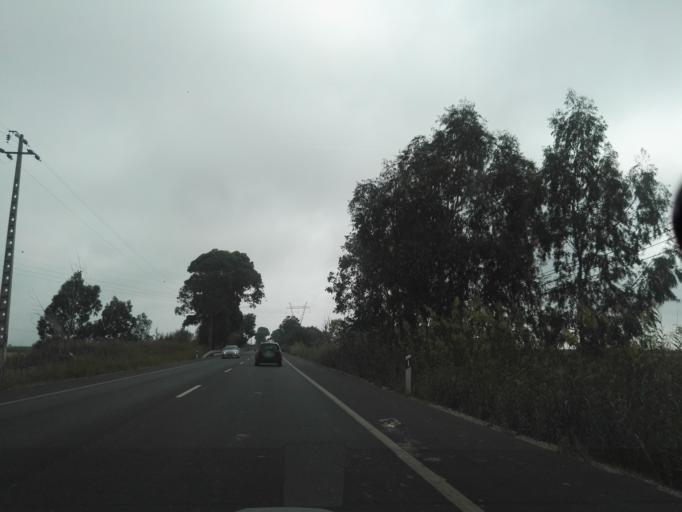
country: PT
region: Lisbon
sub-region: Vila Franca de Xira
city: Vila Franca de Xira
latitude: 38.9478
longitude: -8.9627
